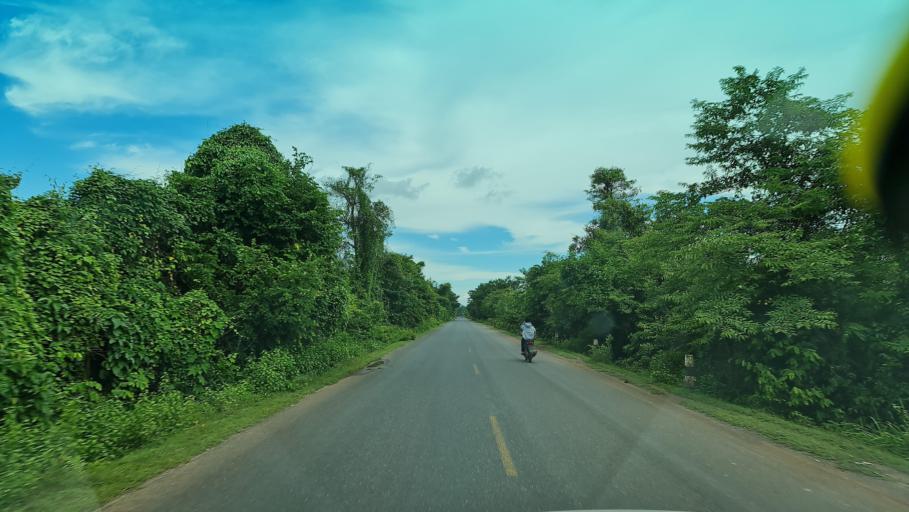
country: TH
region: Nakhon Phanom
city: Ban Phaeng
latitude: 18.0750
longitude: 104.2943
